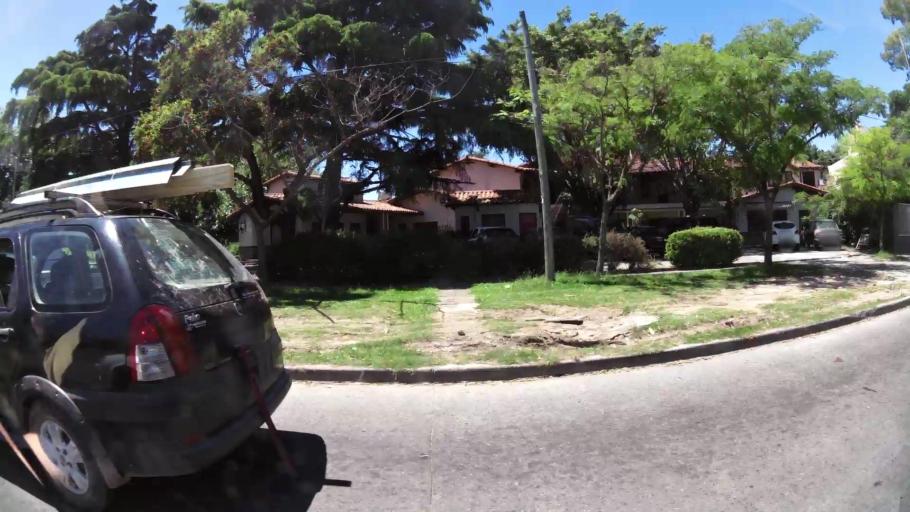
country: AR
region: Buenos Aires
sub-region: Partido de San Isidro
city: San Isidro
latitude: -34.4950
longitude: -58.5587
